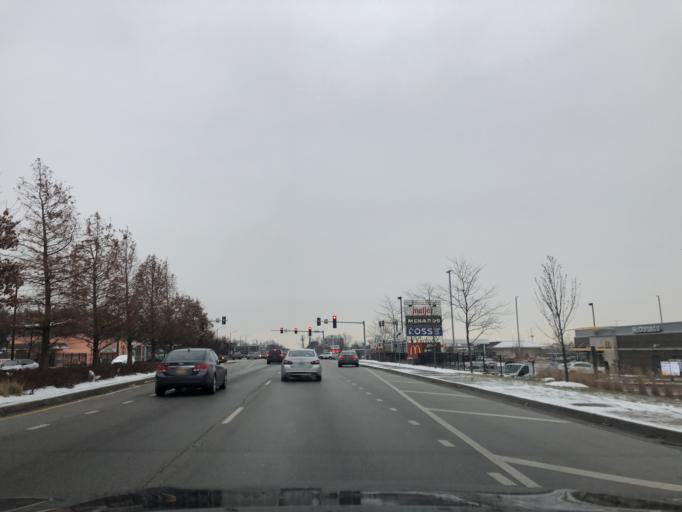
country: US
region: Illinois
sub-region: Cook County
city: Evergreen Park
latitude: 41.7263
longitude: -87.6824
